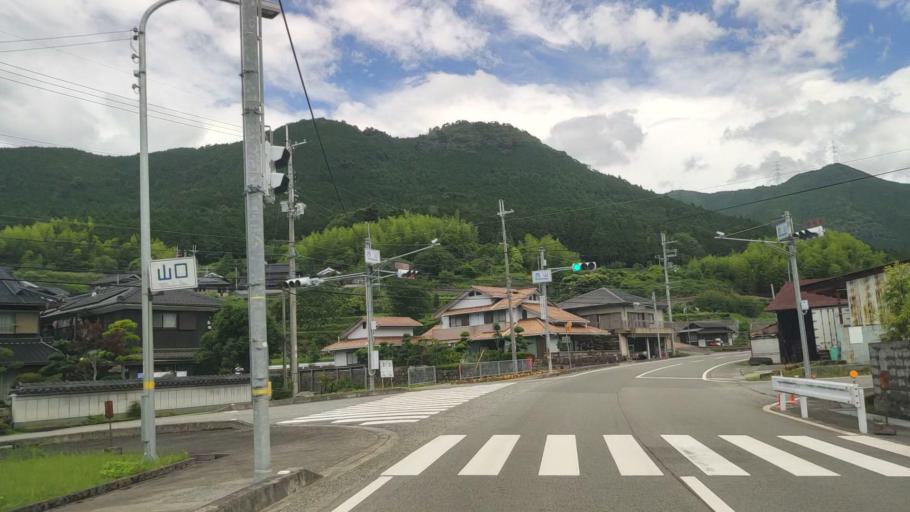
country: JP
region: Hyogo
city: Nishiwaki
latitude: 35.1466
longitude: 134.9248
